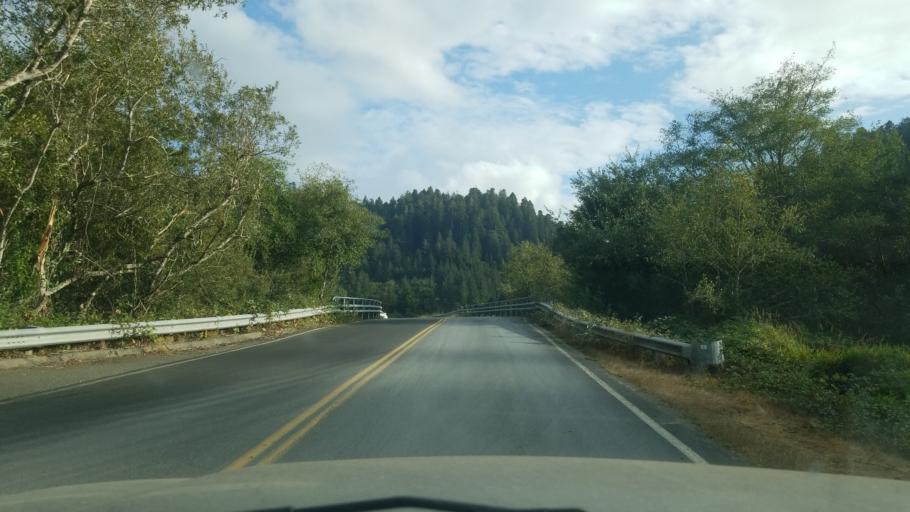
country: US
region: California
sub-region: Humboldt County
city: Westhaven-Moonstone
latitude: 41.3227
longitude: -124.0430
